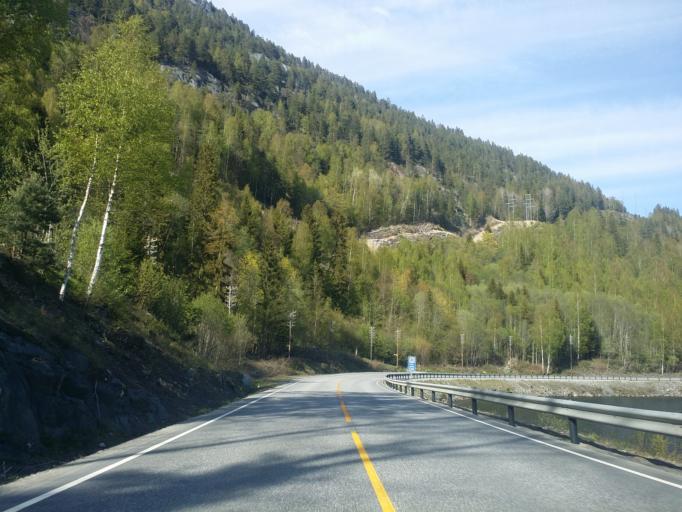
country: NO
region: Telemark
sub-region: Seljord
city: Seljord
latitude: 59.6094
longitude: 8.7510
